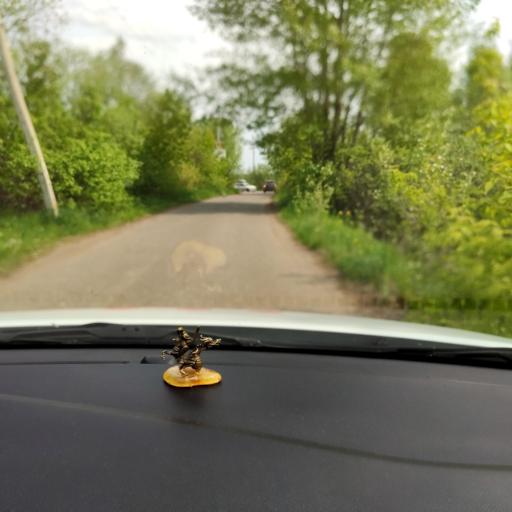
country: RU
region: Tatarstan
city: Verkhniy Uslon
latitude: 55.6958
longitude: 49.0533
